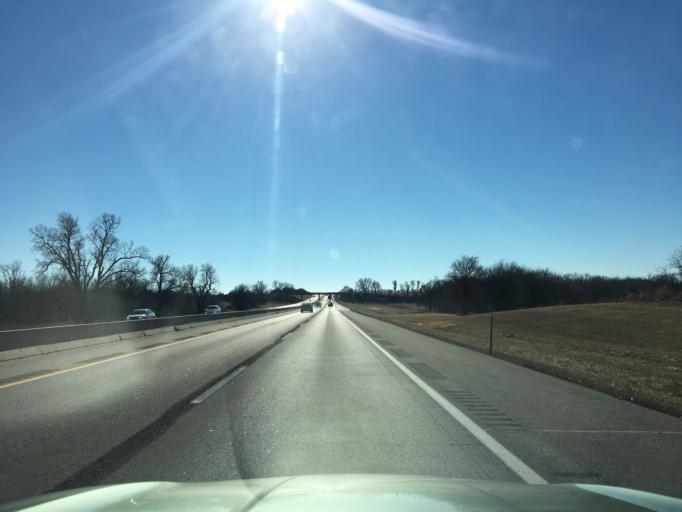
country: US
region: Kansas
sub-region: Sumner County
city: Wellington
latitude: 37.0910
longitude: -97.3387
